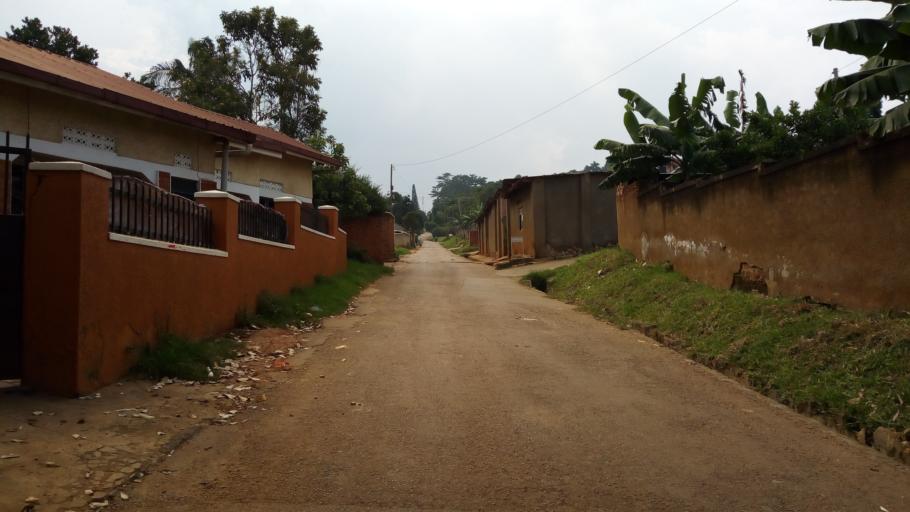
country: UG
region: Central Region
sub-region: Wakiso District
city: Kireka
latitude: 0.3103
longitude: 32.6415
